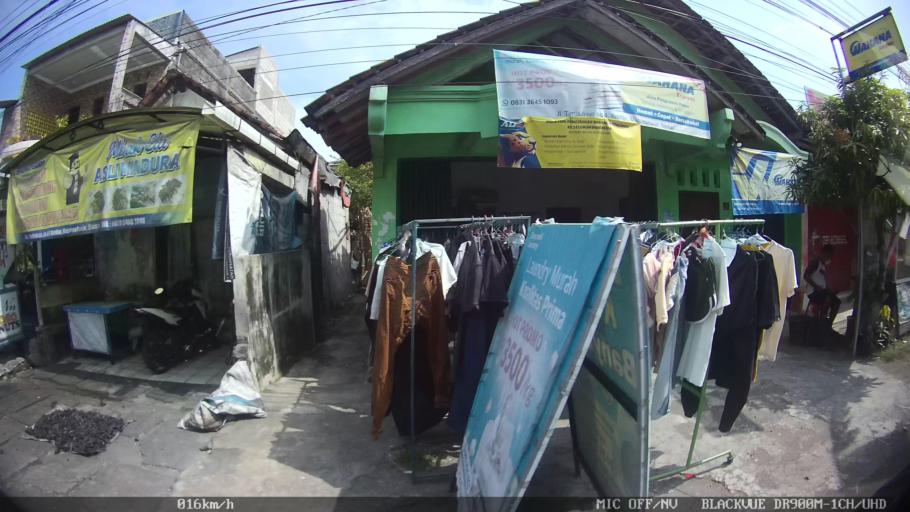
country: ID
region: Daerah Istimewa Yogyakarta
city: Depok
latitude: -7.7593
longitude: 110.4232
